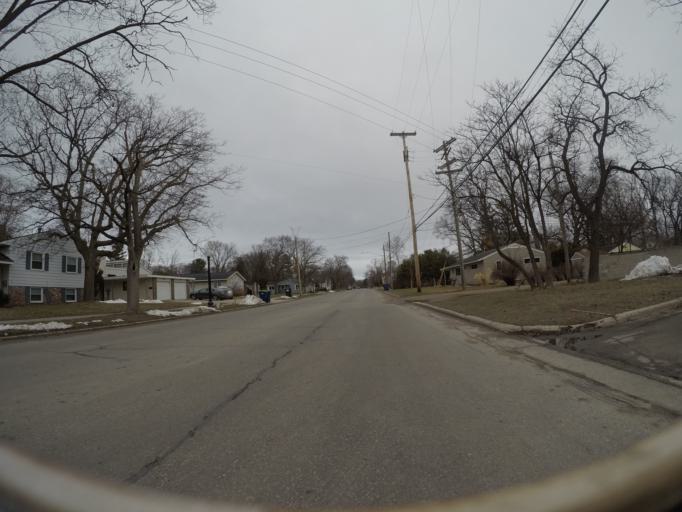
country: US
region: Michigan
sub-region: Grand Traverse County
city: Traverse City
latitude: 44.7599
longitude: -85.6004
